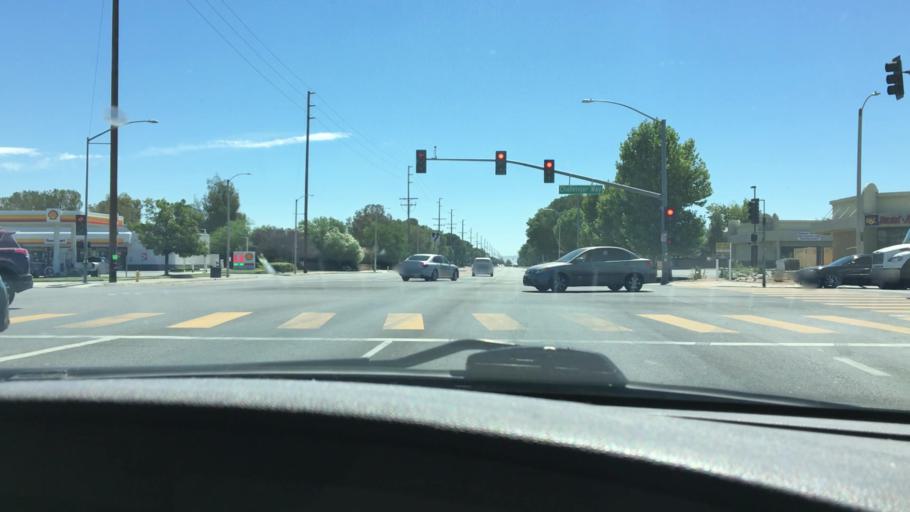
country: US
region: California
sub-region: Los Angeles County
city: Lancaster
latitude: 34.6749
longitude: -118.1127
